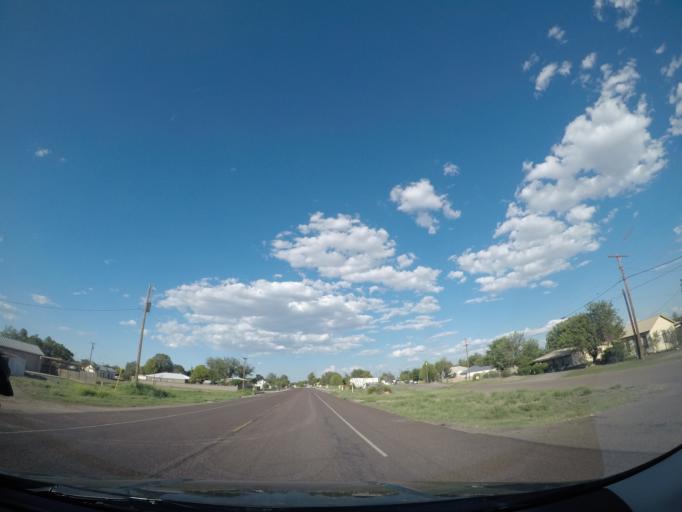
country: US
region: Texas
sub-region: Presidio County
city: Marfa
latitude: 30.3063
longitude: -104.0334
